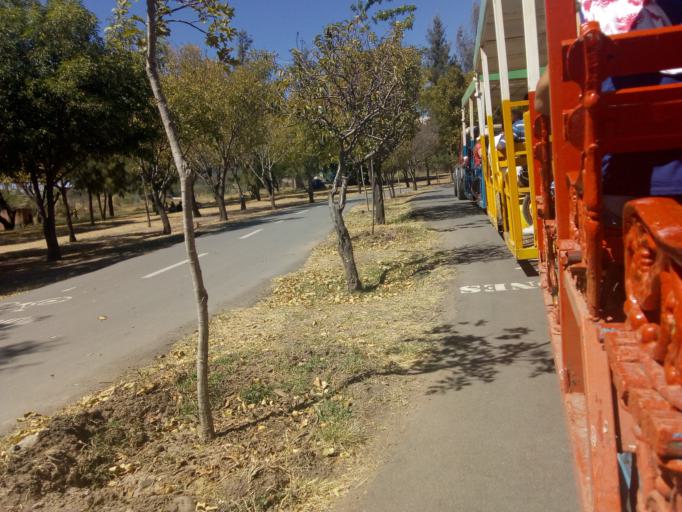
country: MX
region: Guanajuato
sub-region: Leon
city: La Ermita
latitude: 21.1883
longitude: -101.6860
